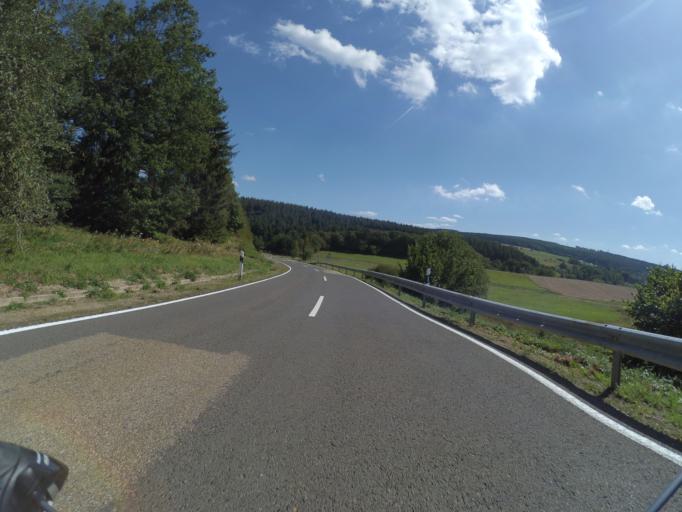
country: DE
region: Rheinland-Pfalz
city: Herl
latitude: 49.7294
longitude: 6.8238
